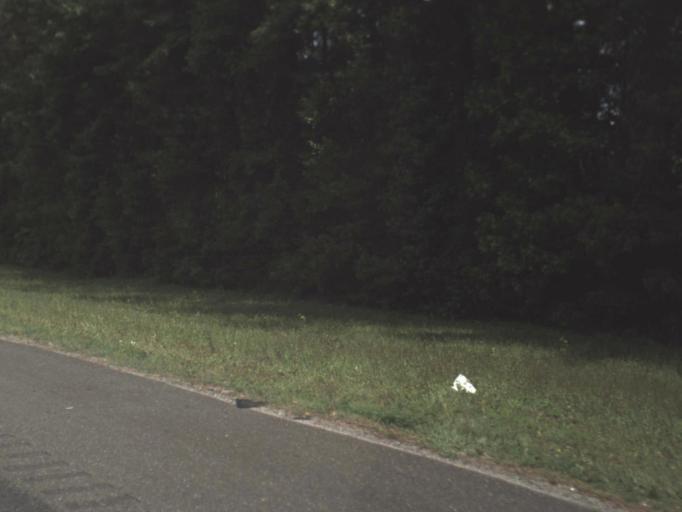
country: US
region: Florida
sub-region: Nassau County
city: Nassau Village-Ratliff
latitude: 30.4516
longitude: -81.7135
